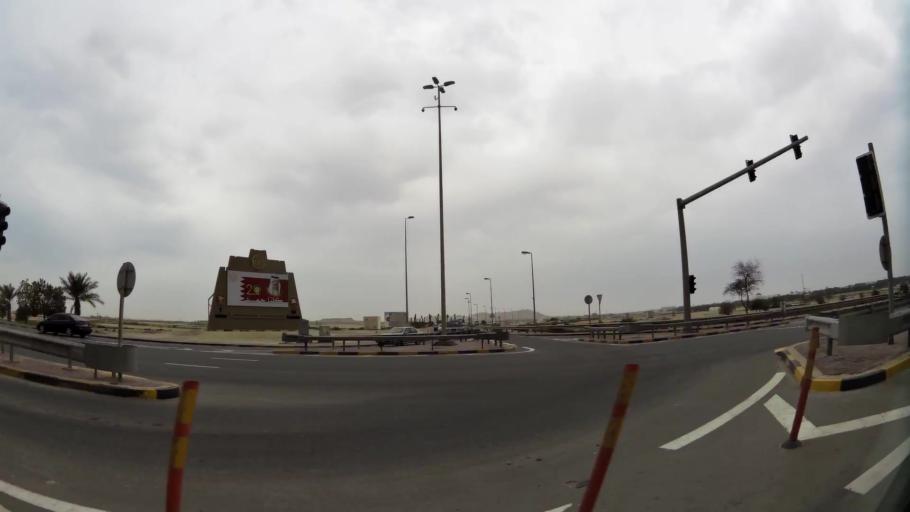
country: BH
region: Central Governorate
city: Dar Kulayb
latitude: 26.0756
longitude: 50.5352
